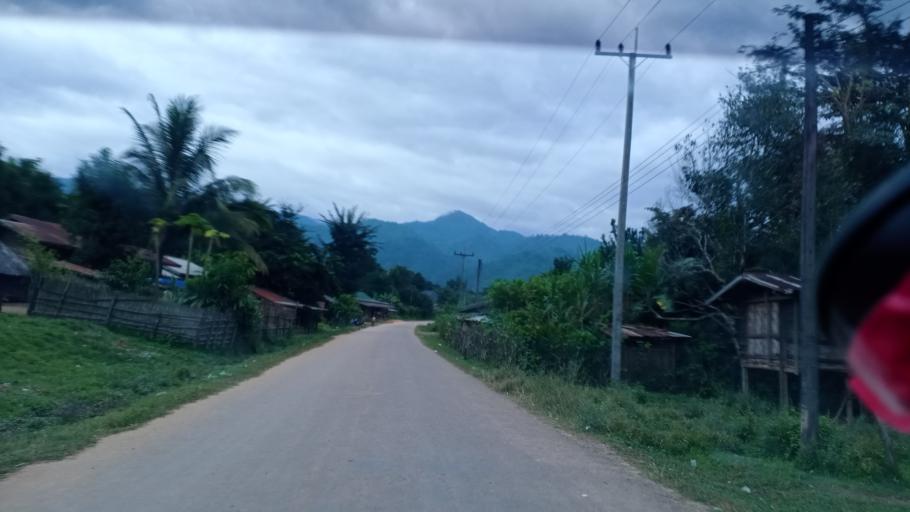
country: TH
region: Changwat Bueng Kan
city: Pak Khat
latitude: 18.7102
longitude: 103.2113
